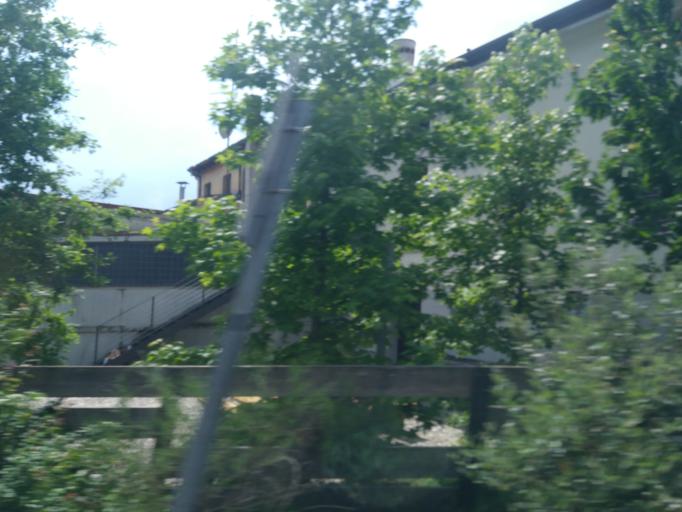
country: IT
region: Veneto
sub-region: Provincia di Vicenza
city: Dueville
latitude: 45.6335
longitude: 11.5475
